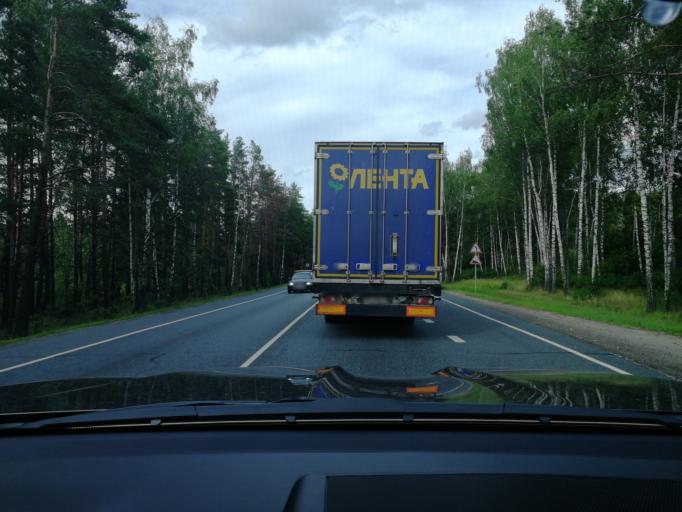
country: RU
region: Moskovskaya
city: Popovo
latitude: 55.0486
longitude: 37.7555
